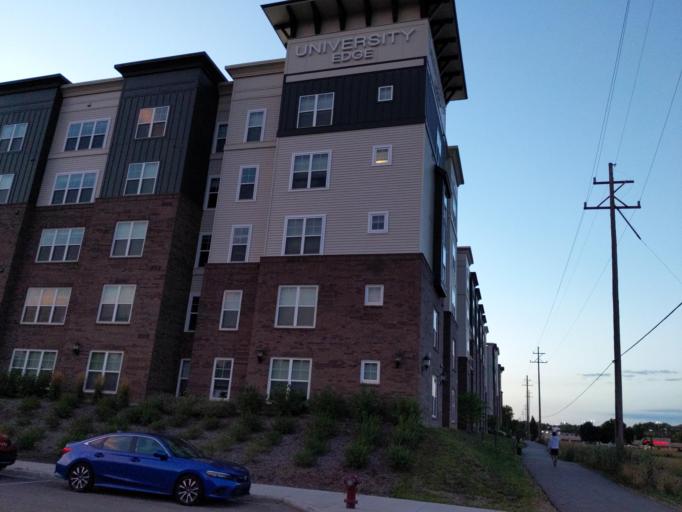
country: US
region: Michigan
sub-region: Ingham County
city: East Lansing
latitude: 42.7314
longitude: -84.5037
